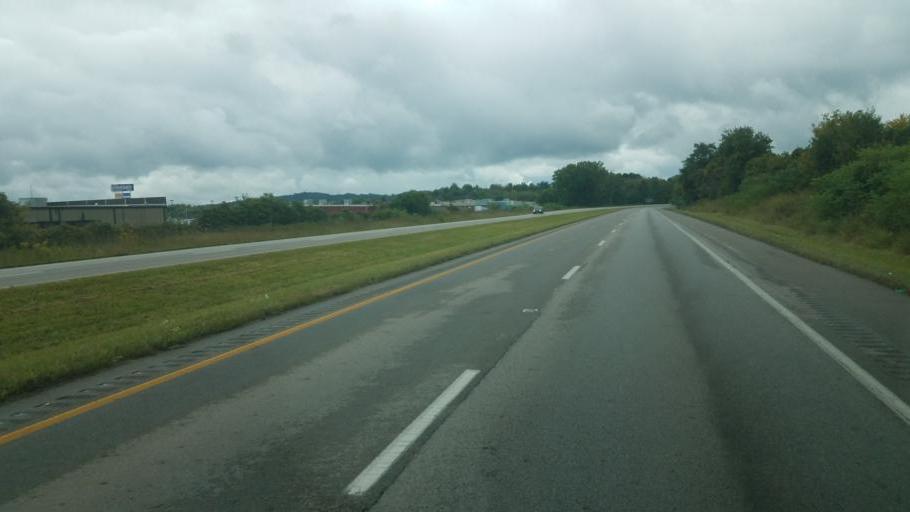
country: US
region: Ohio
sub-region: Scioto County
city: Wheelersburg
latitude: 38.7167
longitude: -82.8595
